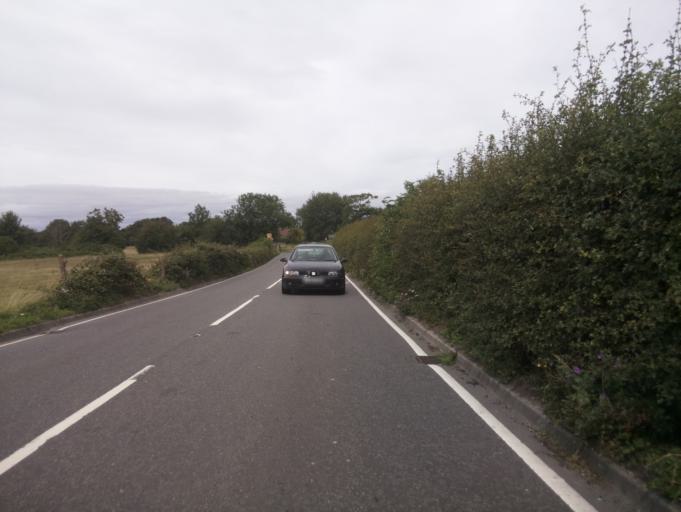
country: GB
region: England
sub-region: North Somerset
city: Kenn
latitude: 51.4018
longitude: -2.8422
